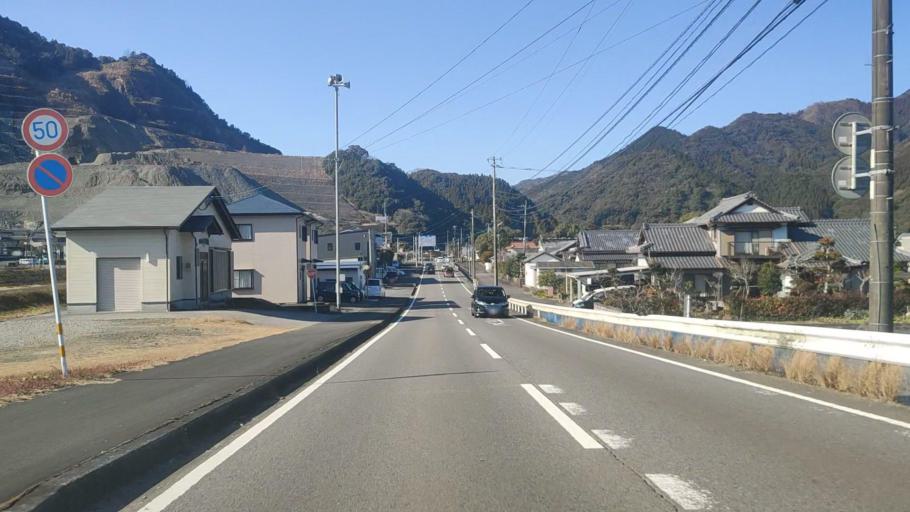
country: JP
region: Oita
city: Saiki
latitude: 32.9791
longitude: 131.8502
